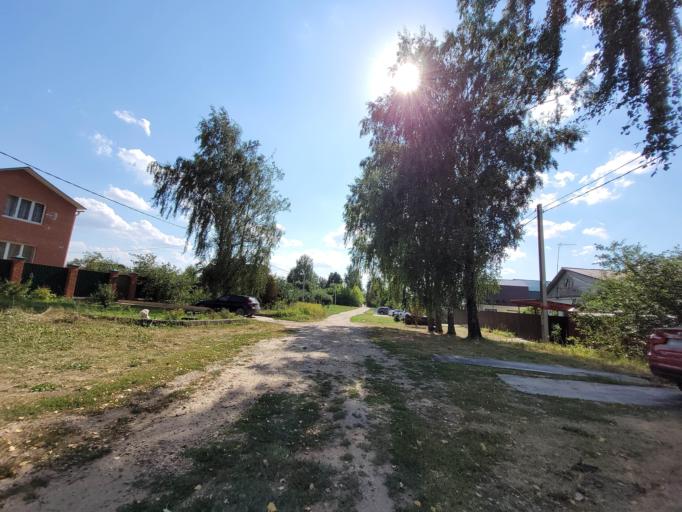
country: RU
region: Moskovskaya
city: Peski
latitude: 55.2330
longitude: 38.7516
